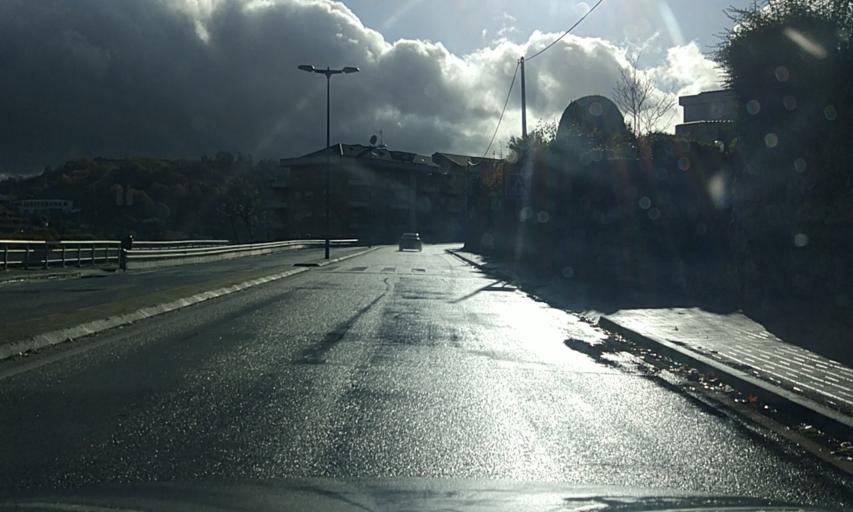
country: PT
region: Viseu
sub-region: Lamego
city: Lamego
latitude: 41.1004
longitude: -7.7999
